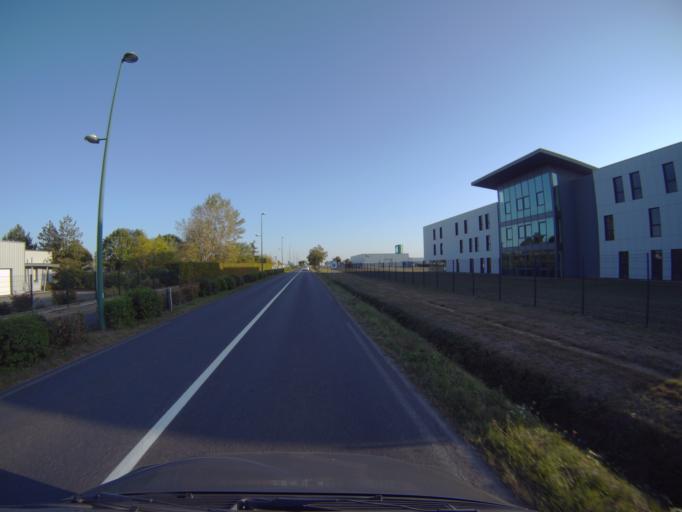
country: FR
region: Pays de la Loire
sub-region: Departement de la Vendee
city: Cugand
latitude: 47.0583
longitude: -1.2556
